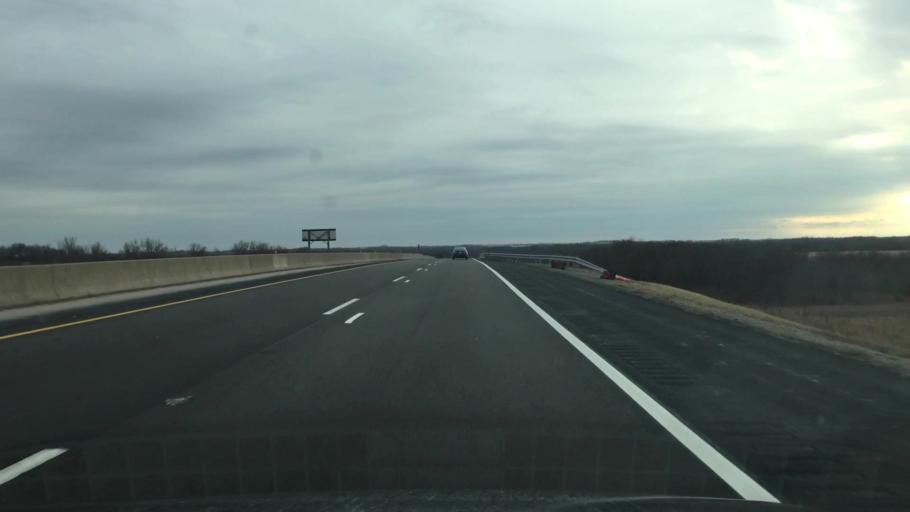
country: US
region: Kansas
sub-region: Osage County
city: Osage City
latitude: 38.6306
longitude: -96.0435
